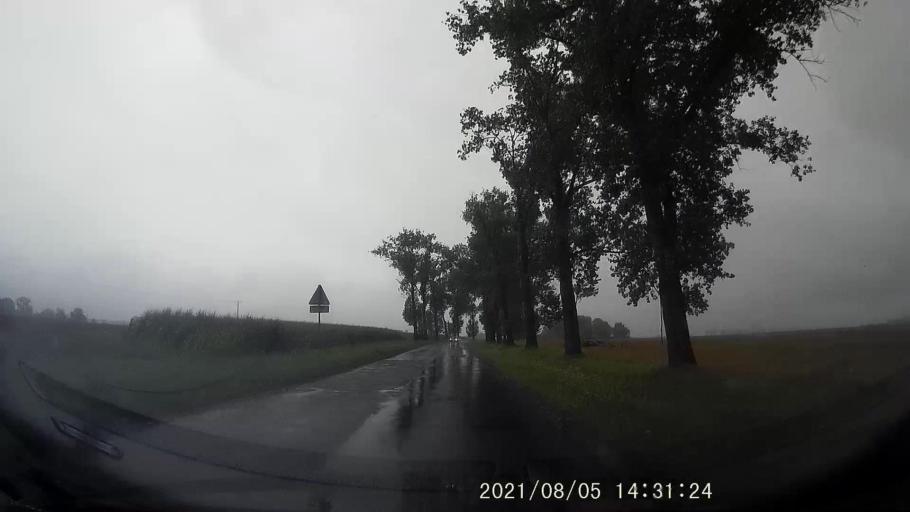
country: PL
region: Opole Voivodeship
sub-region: Powiat nyski
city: Korfantow
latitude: 50.4755
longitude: 17.5574
